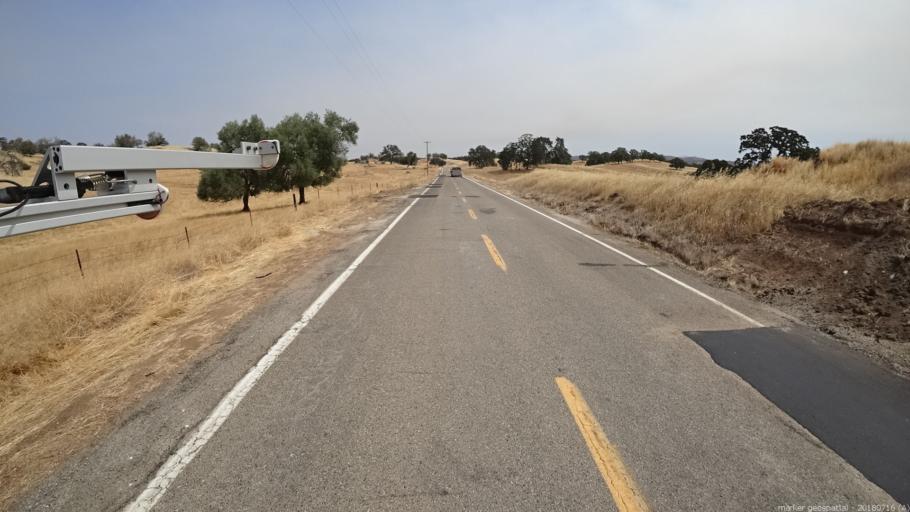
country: US
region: California
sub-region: Madera County
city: Yosemite Lakes
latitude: 37.1553
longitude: -119.9124
